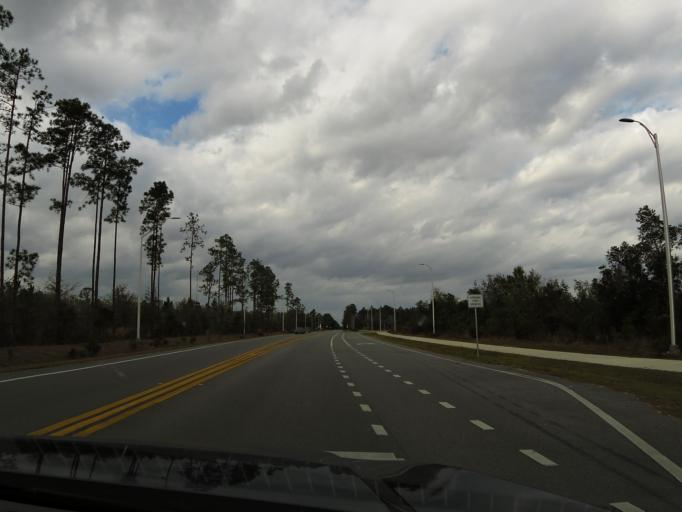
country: US
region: Florida
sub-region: Volusia County
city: Pierson
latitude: 29.2561
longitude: -81.4692
